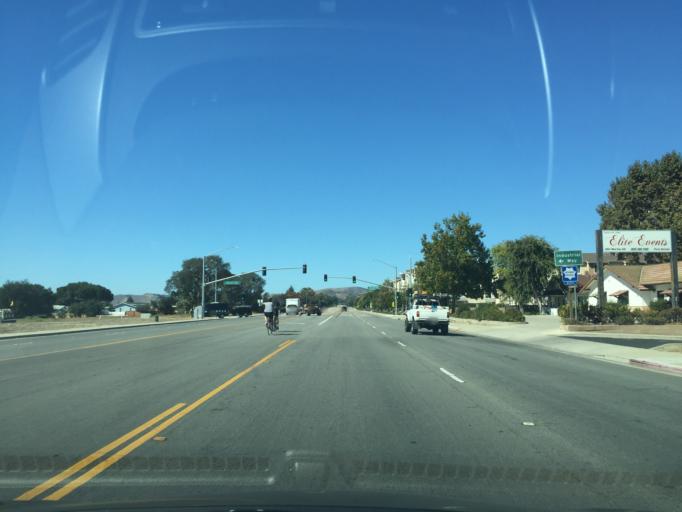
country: US
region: California
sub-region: Santa Barbara County
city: Buellton
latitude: 34.6150
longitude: -120.1976
